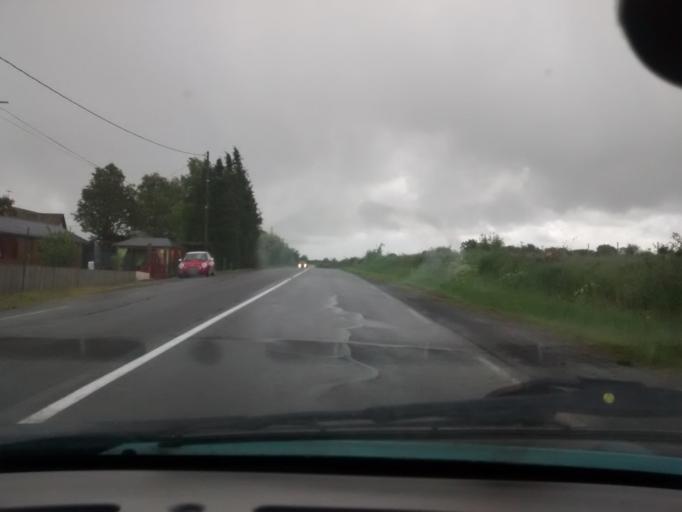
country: FR
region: Lower Normandy
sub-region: Departement de la Manche
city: Conde-sur-Vire
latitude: 49.0891
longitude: -1.0437
